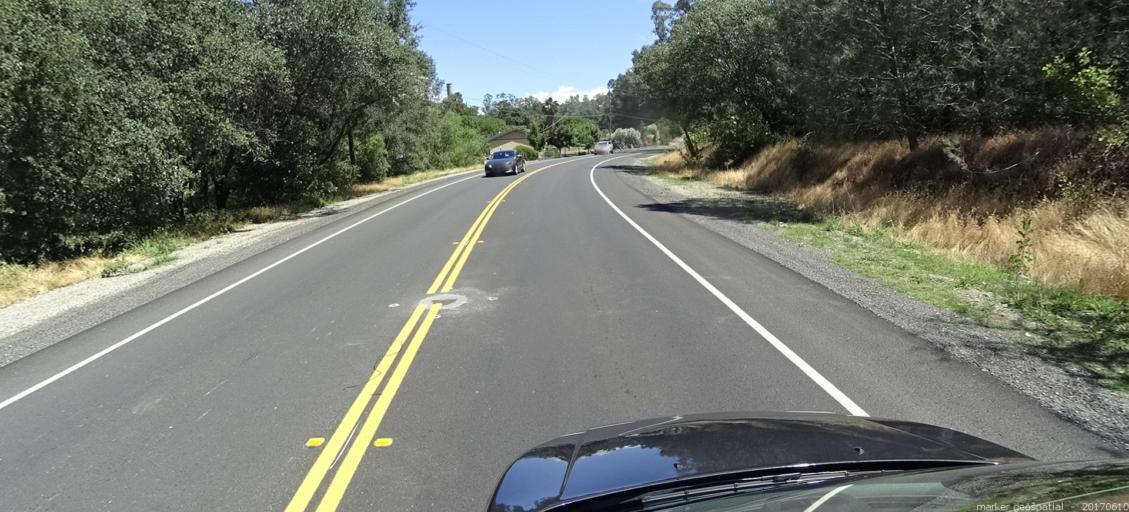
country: US
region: California
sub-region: Butte County
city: Oroville East
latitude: 39.5222
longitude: -121.4844
